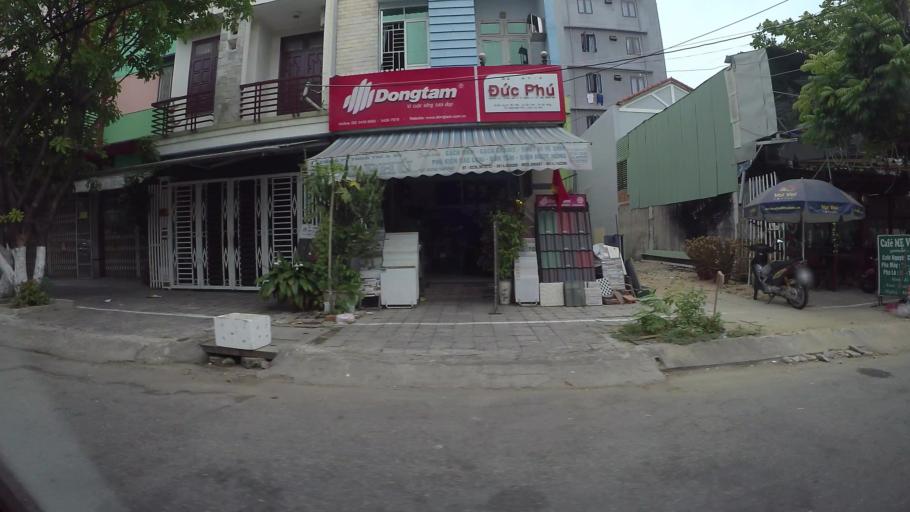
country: VN
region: Da Nang
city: Cam Le
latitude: 16.0330
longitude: 108.2147
